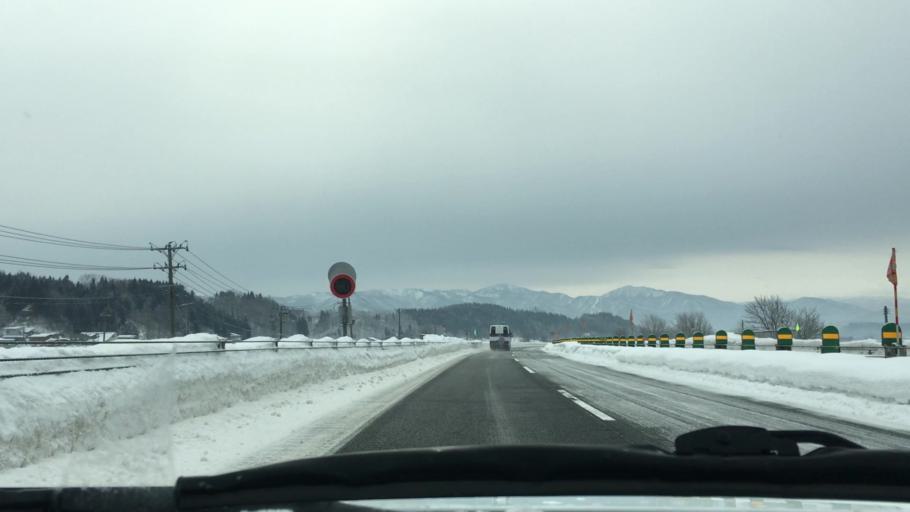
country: JP
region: Akita
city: Hanawa
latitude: 40.2944
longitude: 140.7555
